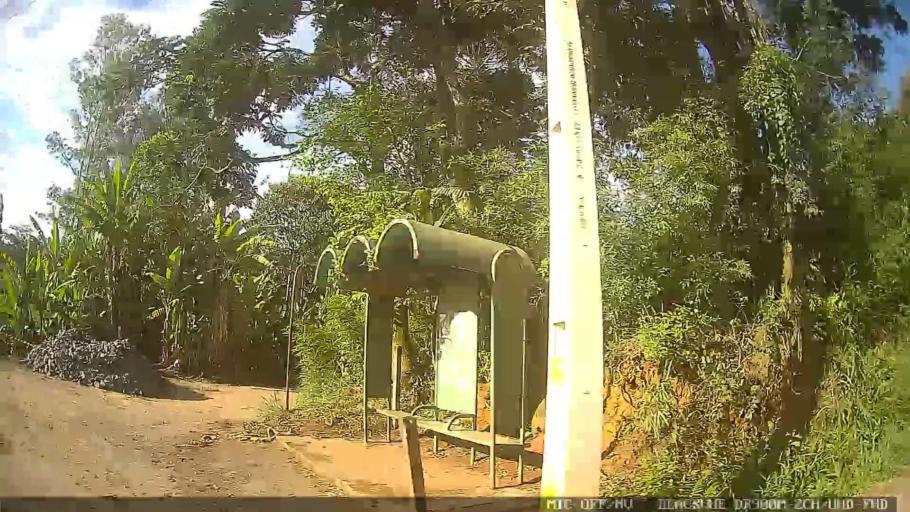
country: BR
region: Minas Gerais
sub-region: Extrema
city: Extrema
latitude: -22.8471
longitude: -46.2779
